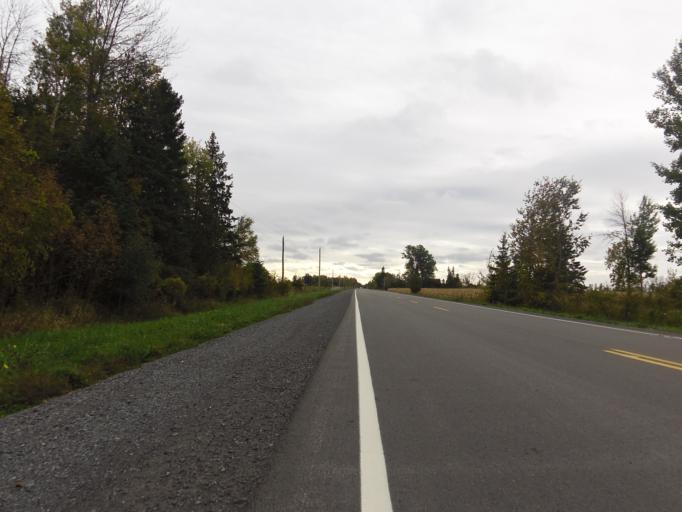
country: CA
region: Ontario
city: Arnprior
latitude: 45.4879
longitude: -76.1893
